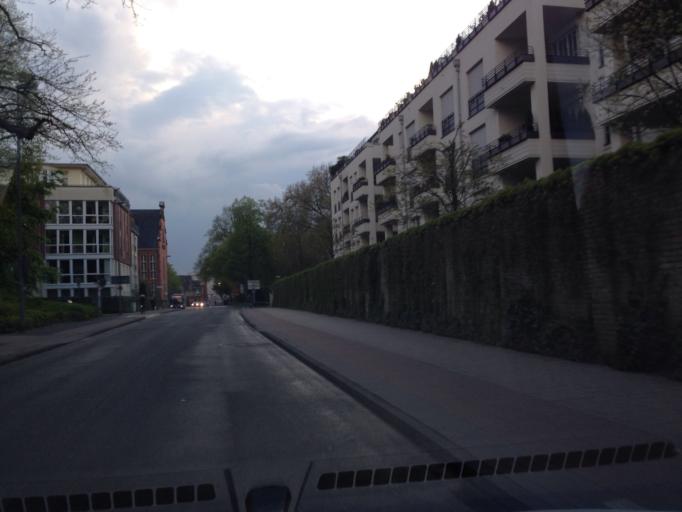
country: DE
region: North Rhine-Westphalia
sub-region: Regierungsbezirk Munster
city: Muenster
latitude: 51.9661
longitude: 7.6369
